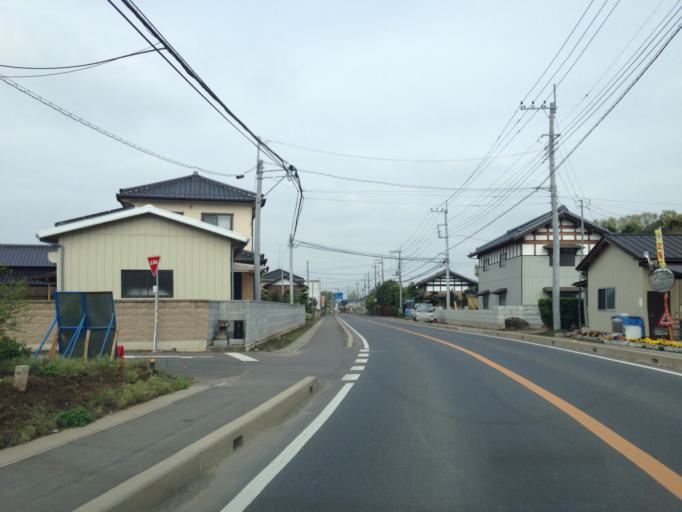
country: JP
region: Ibaraki
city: Ishige
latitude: 36.1578
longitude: 139.9374
